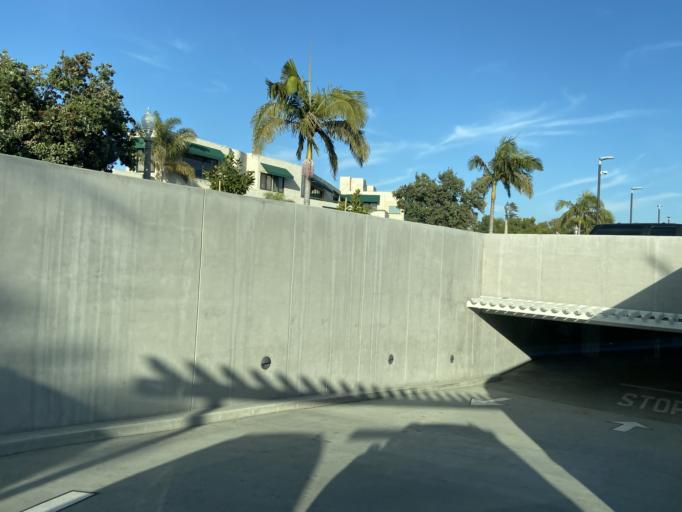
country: US
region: California
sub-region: San Diego County
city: Coronado
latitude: 32.6819
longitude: -117.1797
